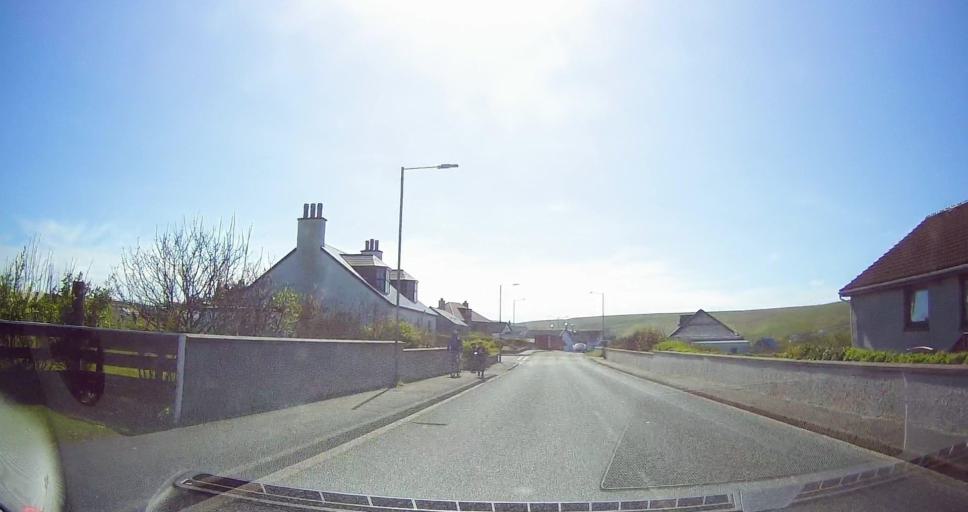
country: GB
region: Scotland
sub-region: Shetland Islands
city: Sandwick
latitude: 60.0003
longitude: -1.2422
